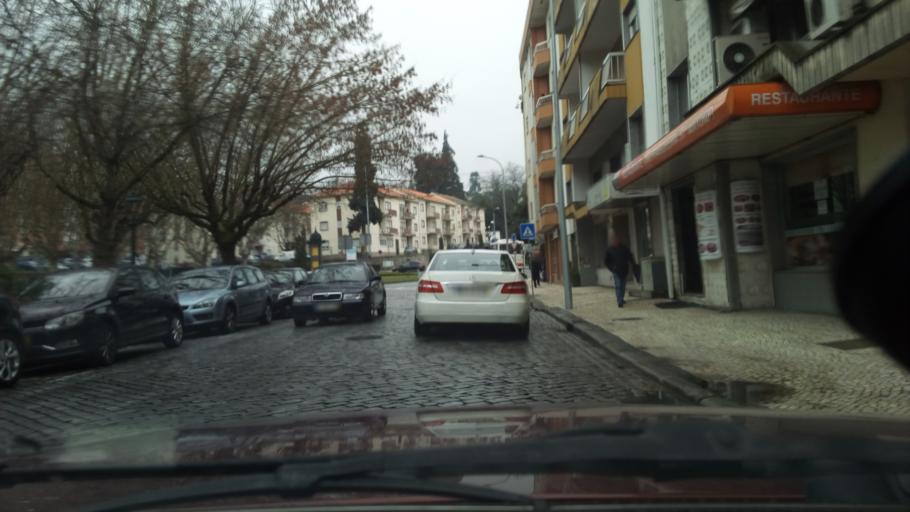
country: PT
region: Viseu
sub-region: Viseu
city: Viseu
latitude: 40.6602
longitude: -7.9078
